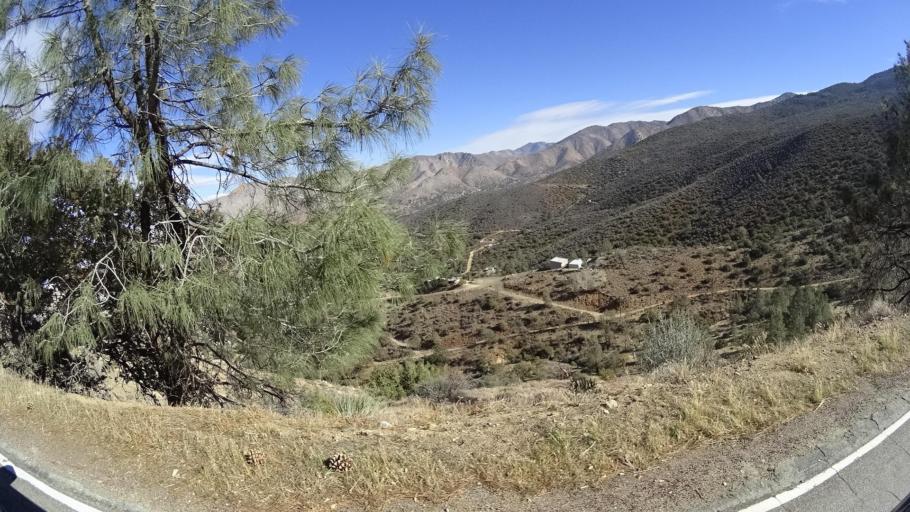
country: US
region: California
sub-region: Kern County
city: Bodfish
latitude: 35.5804
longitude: -118.5045
